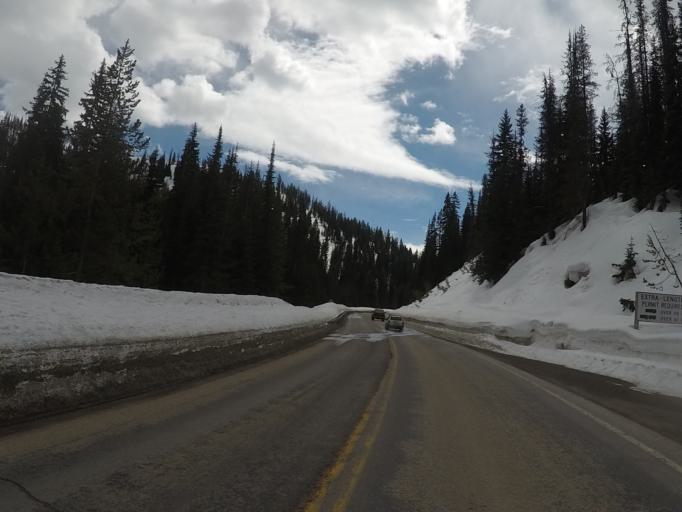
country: US
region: Montana
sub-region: Ravalli County
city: Stevensville
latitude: 46.6462
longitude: -114.5798
